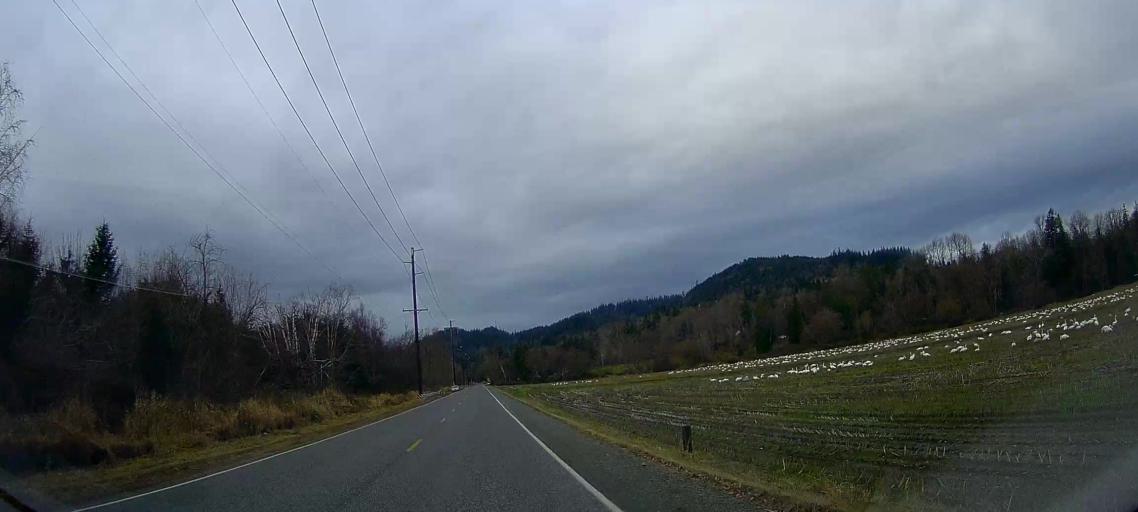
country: US
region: Washington
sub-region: Skagit County
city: Sedro-Woolley
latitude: 48.5257
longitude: -122.2749
